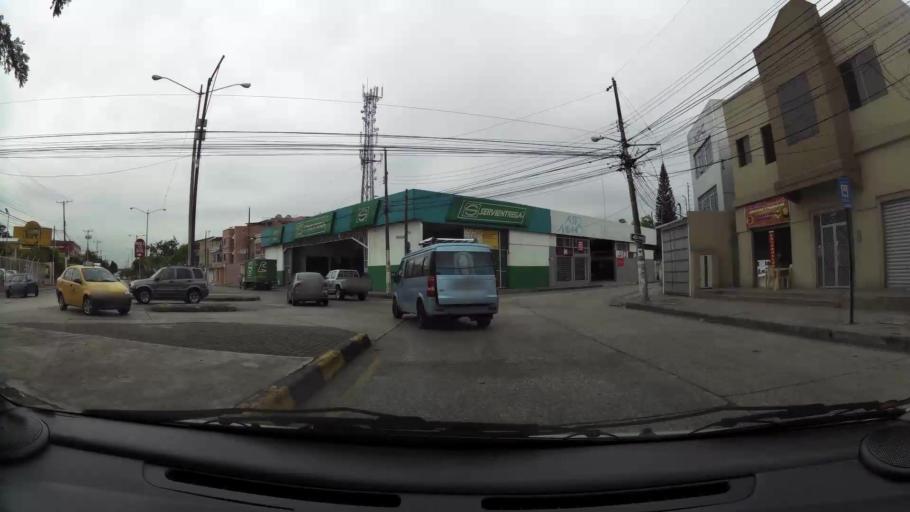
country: EC
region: Guayas
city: Eloy Alfaro
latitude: -2.1514
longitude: -79.8921
